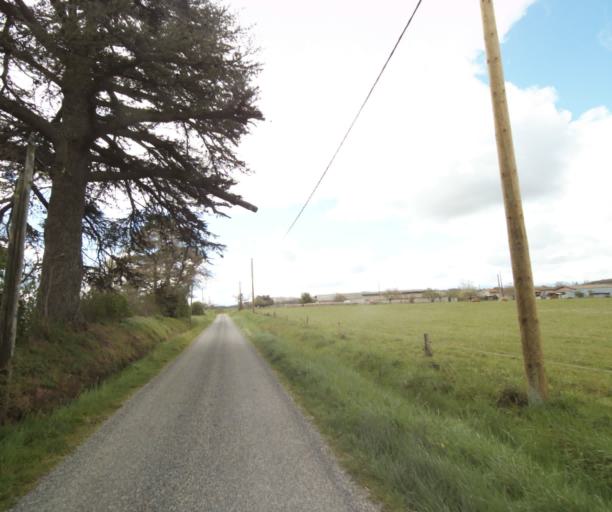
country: FR
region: Midi-Pyrenees
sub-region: Departement de l'Ariege
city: Saverdun
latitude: 43.2148
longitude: 1.5816
